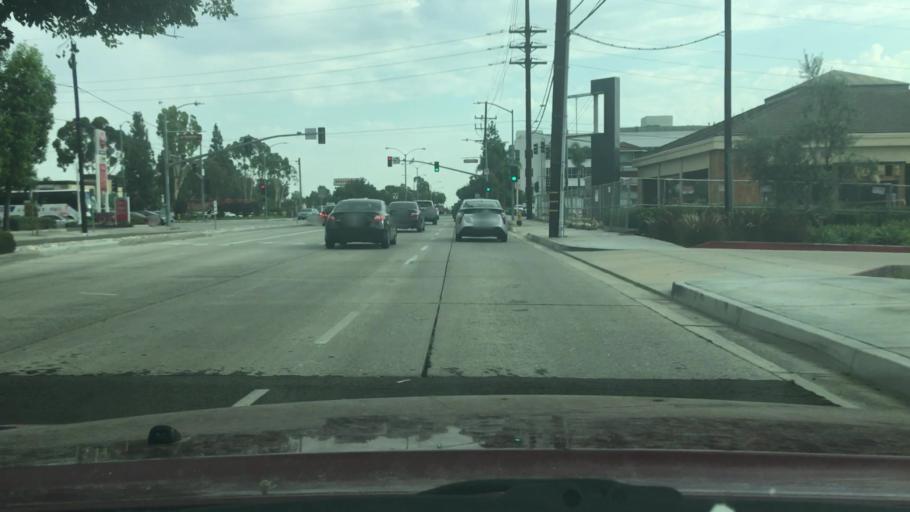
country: US
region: California
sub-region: Los Angeles County
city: La Mirada
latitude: 33.9180
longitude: -118.0120
